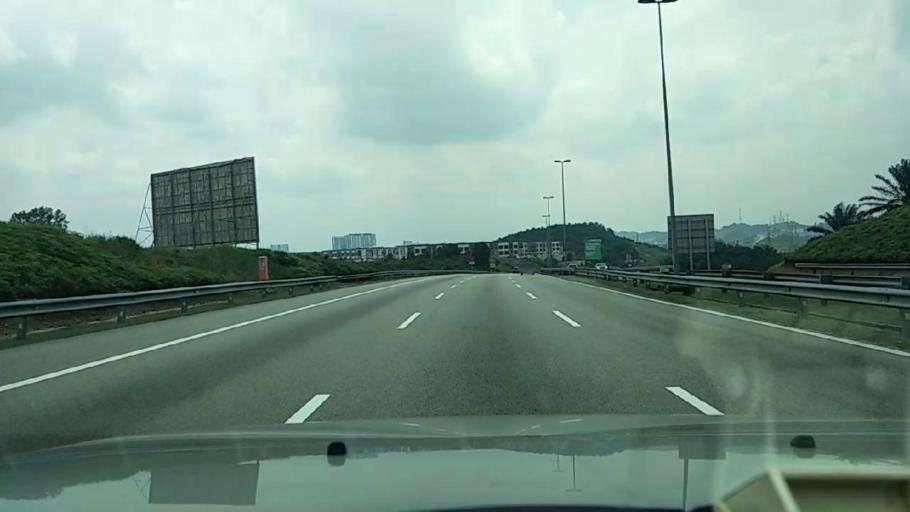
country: MY
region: Putrajaya
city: Putrajaya
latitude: 2.9645
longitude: 101.6567
